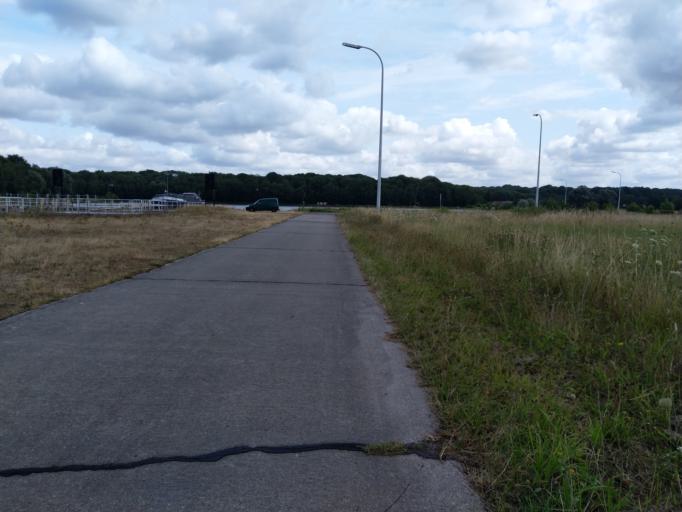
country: BE
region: Wallonia
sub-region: Province du Hainaut
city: Hensies
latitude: 50.4763
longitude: 3.7115
